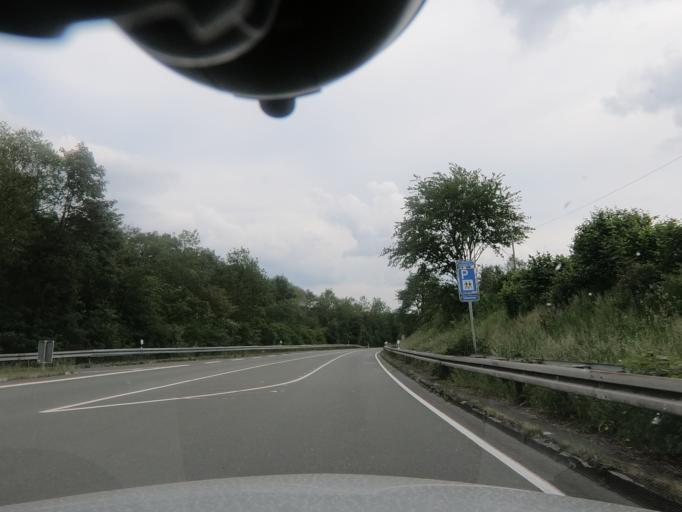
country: DE
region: North Rhine-Westphalia
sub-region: Regierungsbezirk Arnsberg
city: Ruthen
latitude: 51.4339
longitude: 8.4486
